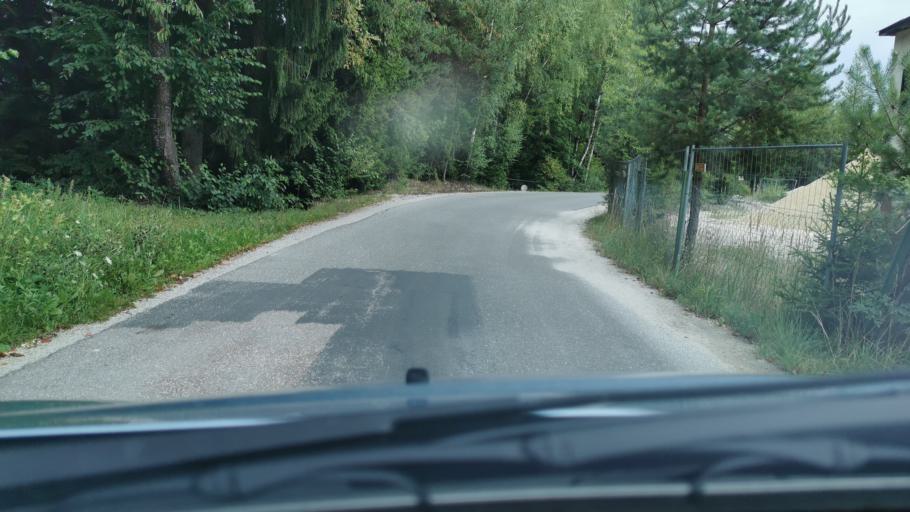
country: AT
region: Styria
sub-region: Politischer Bezirk Weiz
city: Birkfeld
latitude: 47.3922
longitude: 15.6725
